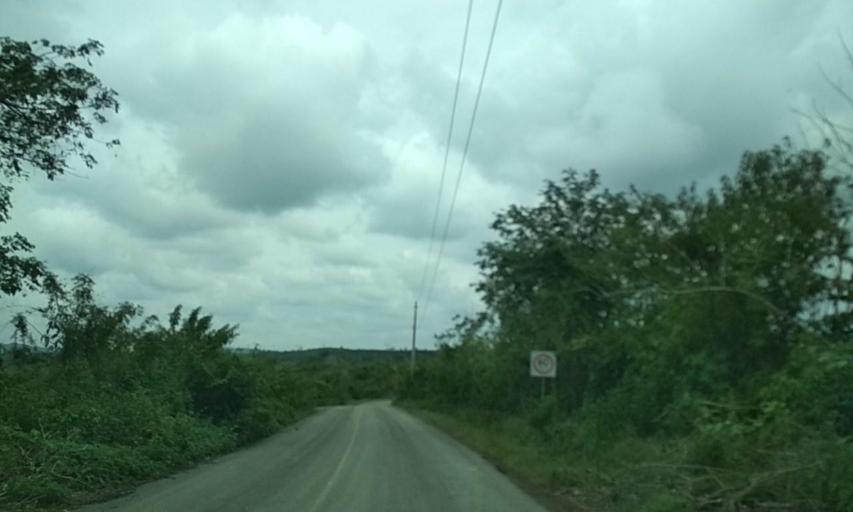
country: MX
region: Puebla
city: Espinal
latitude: 20.3242
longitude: -97.4152
